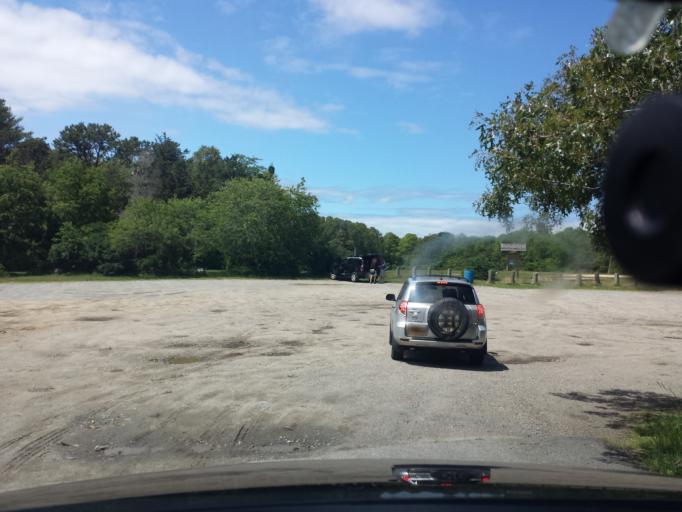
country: US
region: Massachusetts
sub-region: Barnstable County
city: Marstons Mills
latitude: 41.6637
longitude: -70.4056
